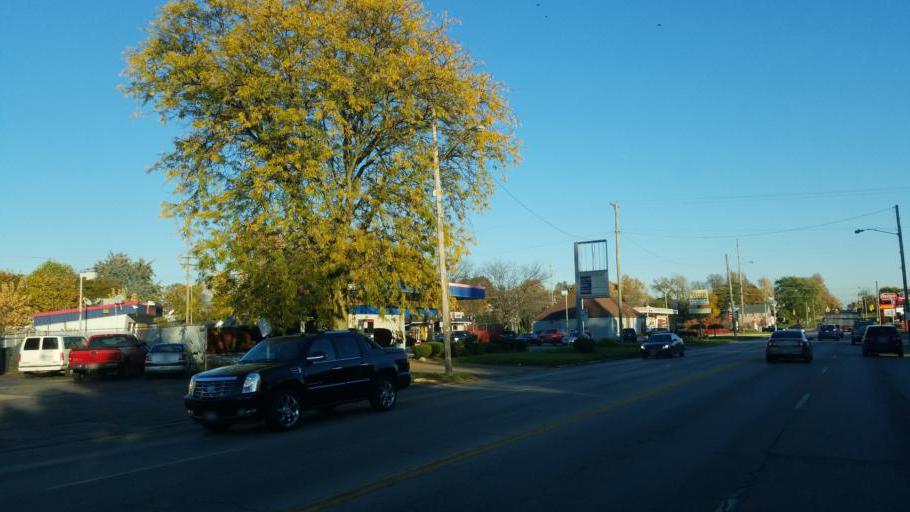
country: US
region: Ohio
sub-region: Sandusky County
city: Fremont
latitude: 41.3455
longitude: -83.1065
